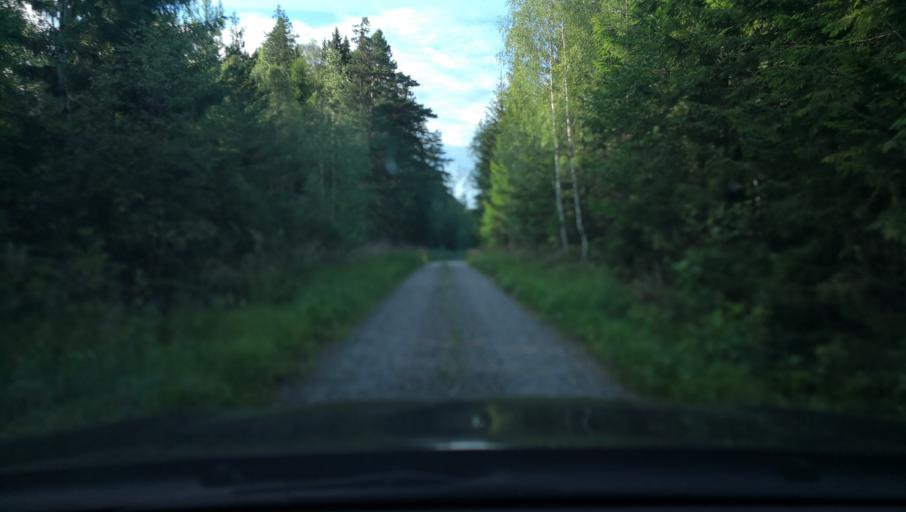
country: SE
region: Uppsala
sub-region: Osthammars Kommun
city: Osterbybruk
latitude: 60.0301
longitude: 17.9180
